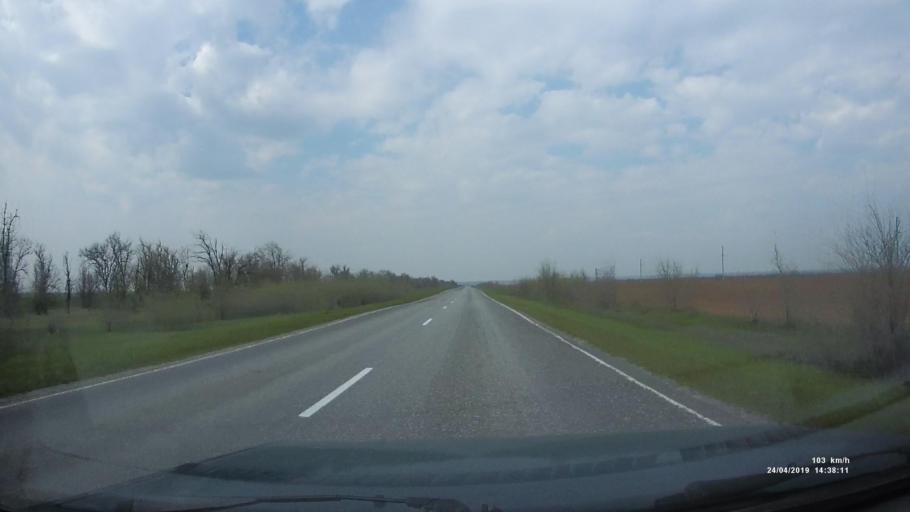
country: RU
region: Rostov
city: Remontnoye
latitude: 46.3973
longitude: 43.8861
